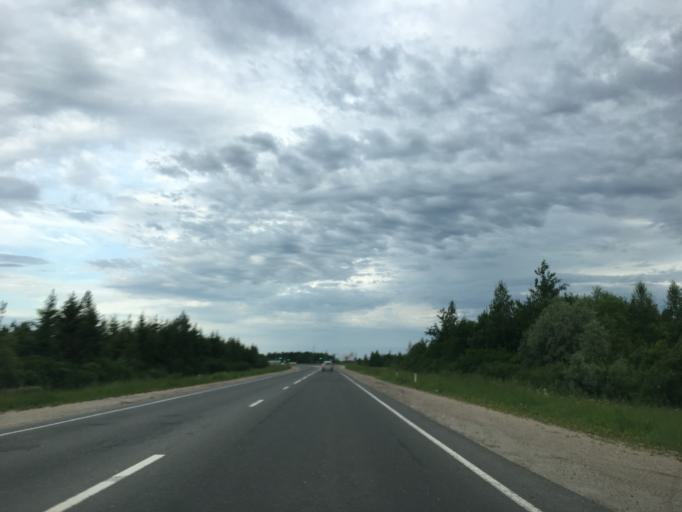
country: RU
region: Pskov
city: Pskov
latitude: 57.8574
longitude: 28.3178
